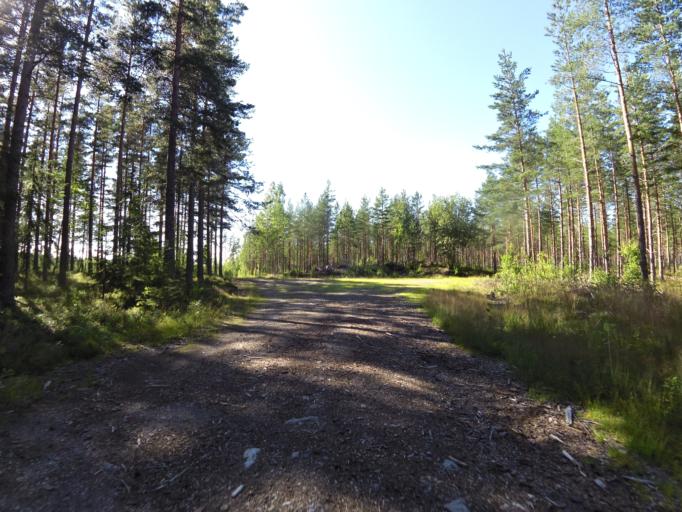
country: SE
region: Gaevleborg
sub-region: Hofors Kommun
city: Hofors
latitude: 60.5726
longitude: 16.4483
